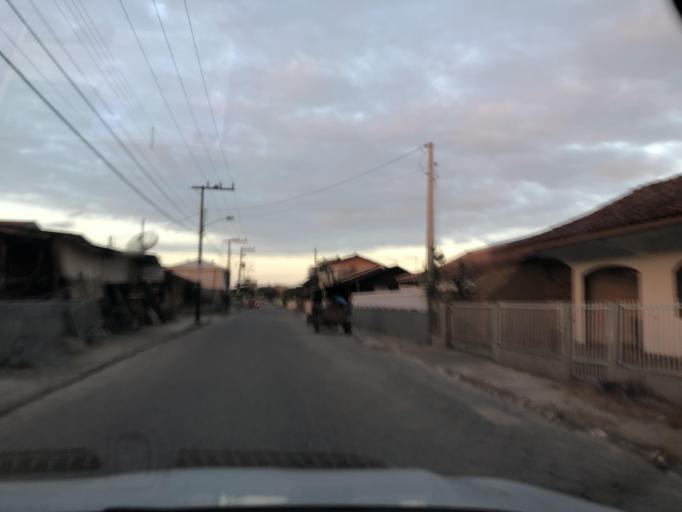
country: BR
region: Santa Catarina
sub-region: Sao Francisco Do Sul
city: Sao Francisco do Sul
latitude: -26.2308
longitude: -48.5089
